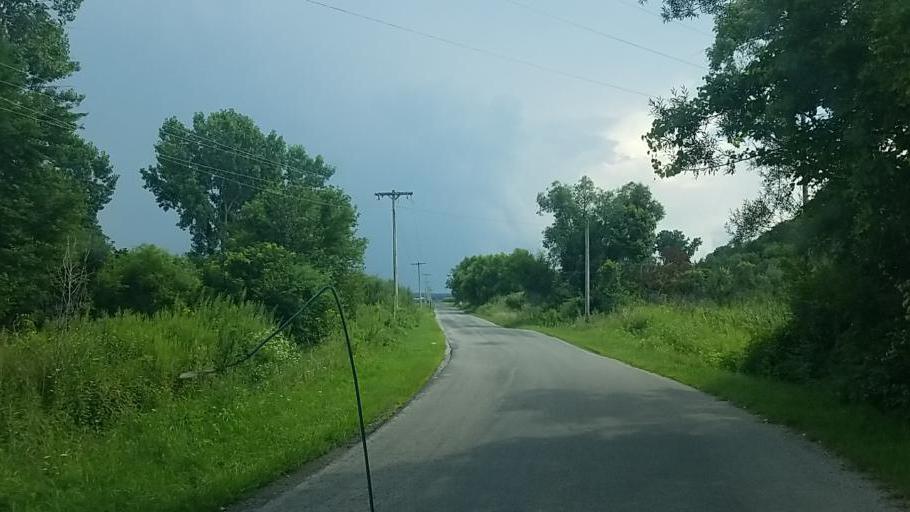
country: US
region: Ohio
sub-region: Medina County
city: Lodi
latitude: 41.0281
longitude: -82.0177
